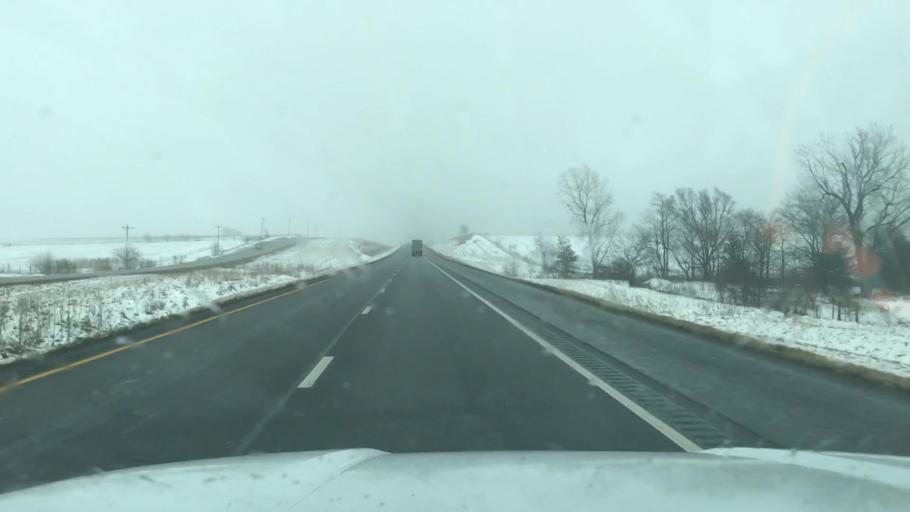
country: US
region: Missouri
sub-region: Clinton County
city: Gower
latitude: 39.7620
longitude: -94.5145
